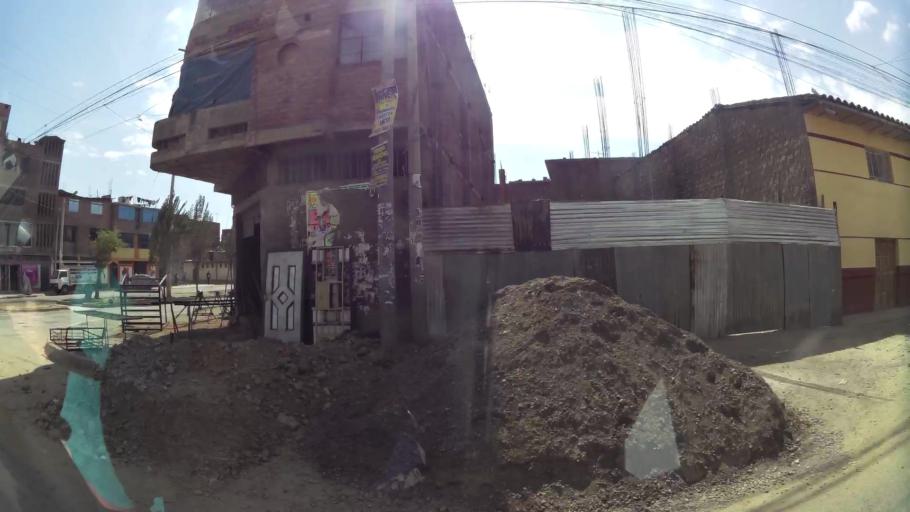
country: PE
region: Junin
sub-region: Provincia de Huancayo
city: Huancayo
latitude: -12.0879
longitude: -75.2028
